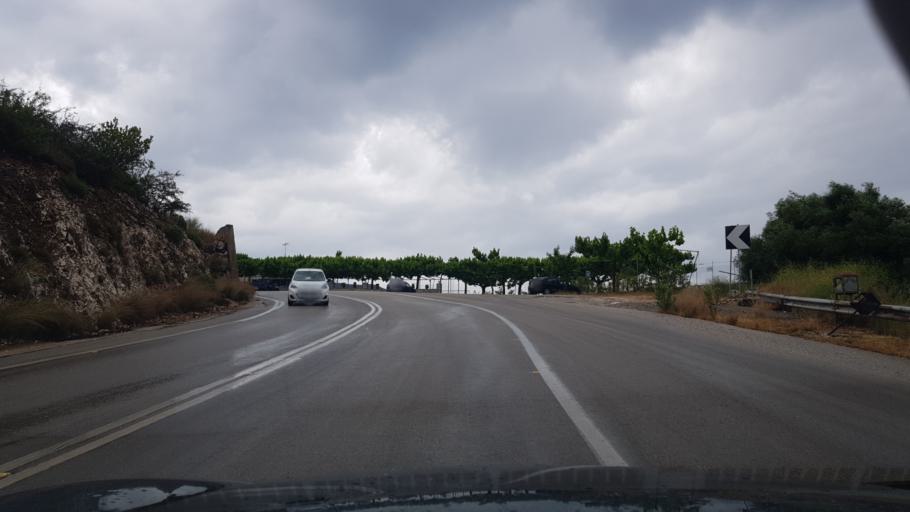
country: GR
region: Ionian Islands
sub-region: Lefkada
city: Nidri
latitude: 38.6329
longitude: 20.6692
